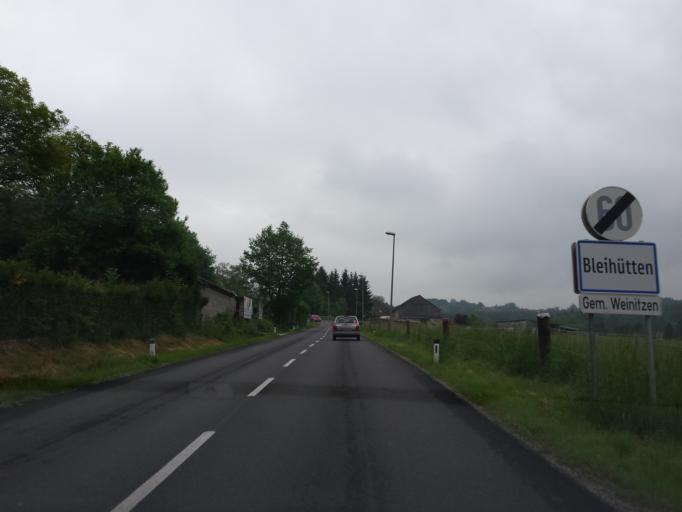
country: AT
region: Styria
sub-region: Politischer Bezirk Graz-Umgebung
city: Kumberg
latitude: 47.1448
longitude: 15.5120
